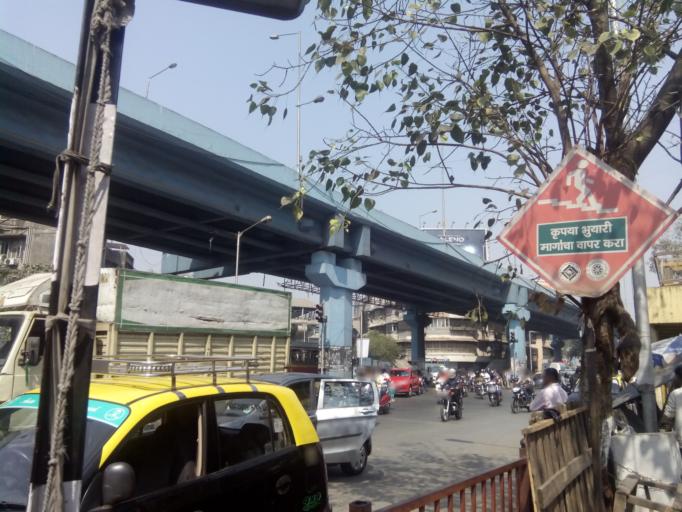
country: IN
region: Maharashtra
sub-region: Mumbai Suburban
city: Mumbai
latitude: 19.0436
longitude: 72.8643
